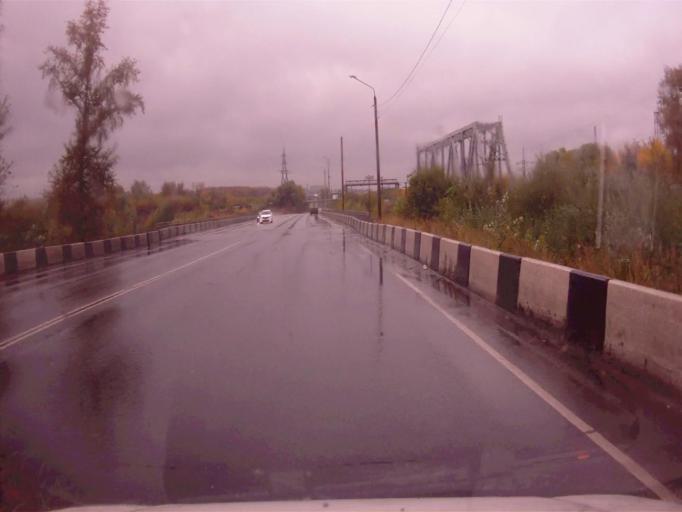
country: RU
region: Chelyabinsk
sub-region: Gorod Chelyabinsk
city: Chelyabinsk
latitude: 55.1987
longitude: 61.4041
